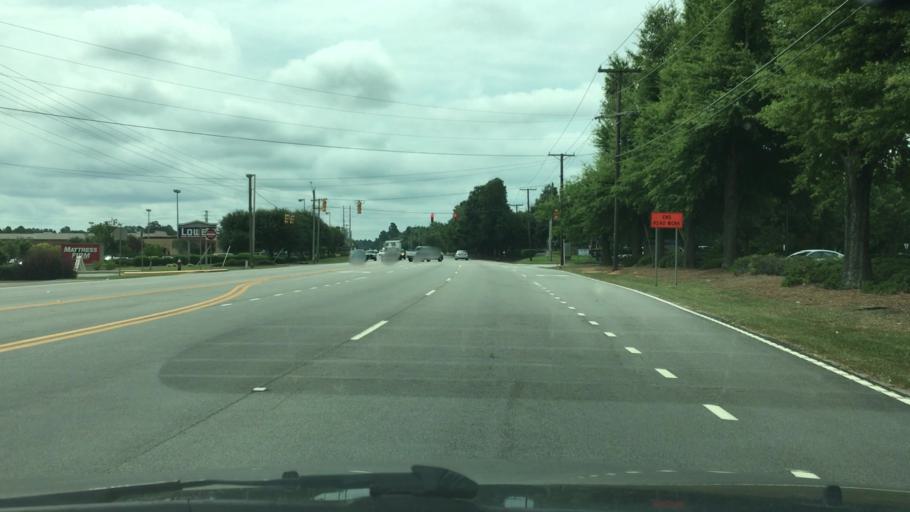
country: US
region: South Carolina
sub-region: Aiken County
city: Aiken
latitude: 33.5097
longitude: -81.7124
